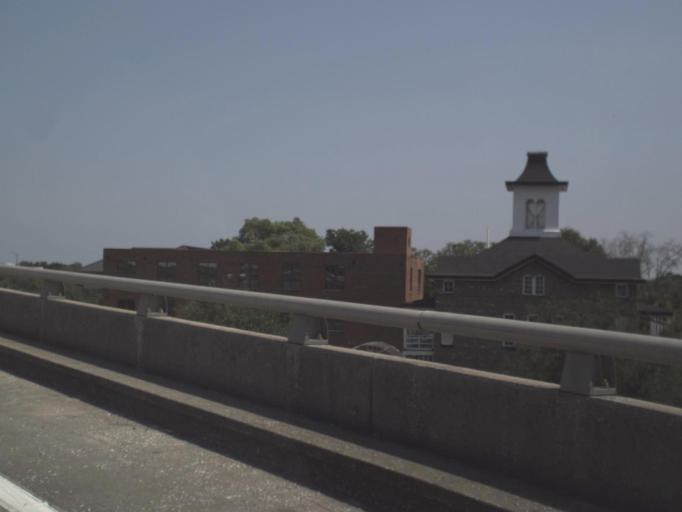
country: US
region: Florida
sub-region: Duval County
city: Jacksonville
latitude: 30.3257
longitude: -81.6471
